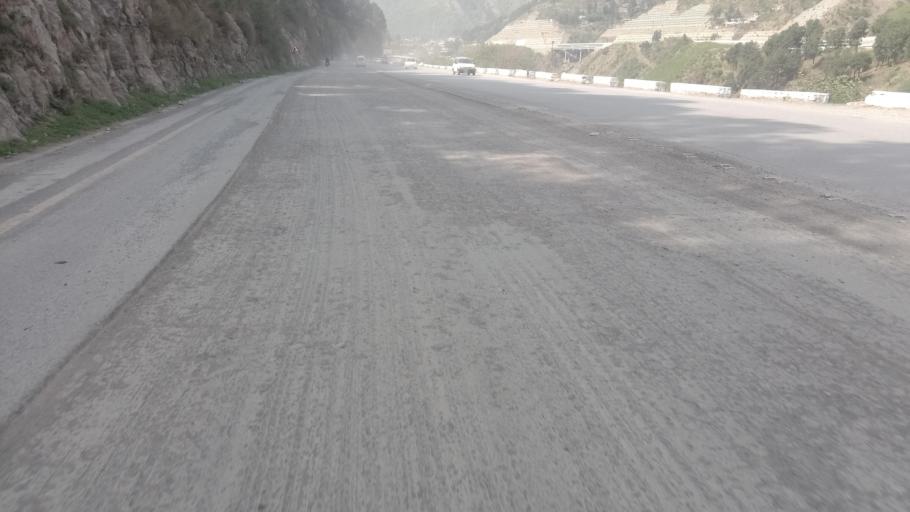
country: PK
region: Khyber Pakhtunkhwa
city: Abbottabad
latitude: 34.1238
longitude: 73.1882
